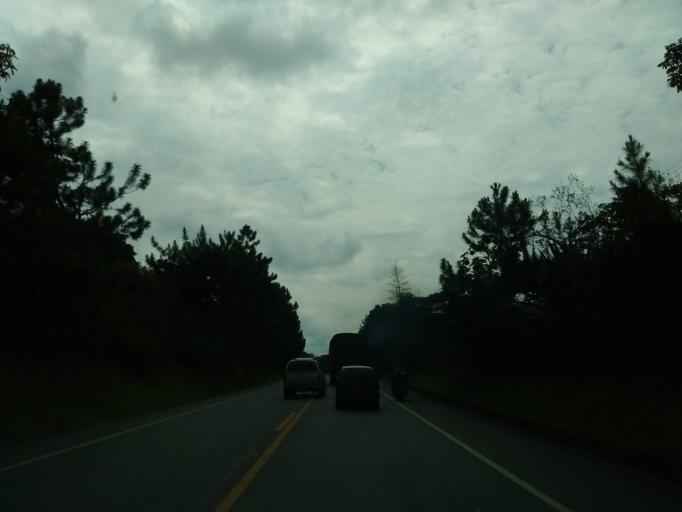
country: CO
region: Cauca
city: Morales
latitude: 2.7695
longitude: -76.5547
